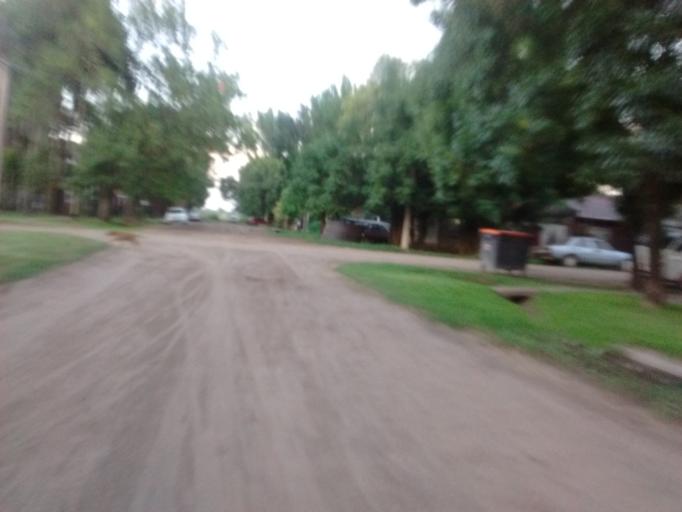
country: AR
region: Santa Fe
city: Funes
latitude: -32.9125
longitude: -60.8178
